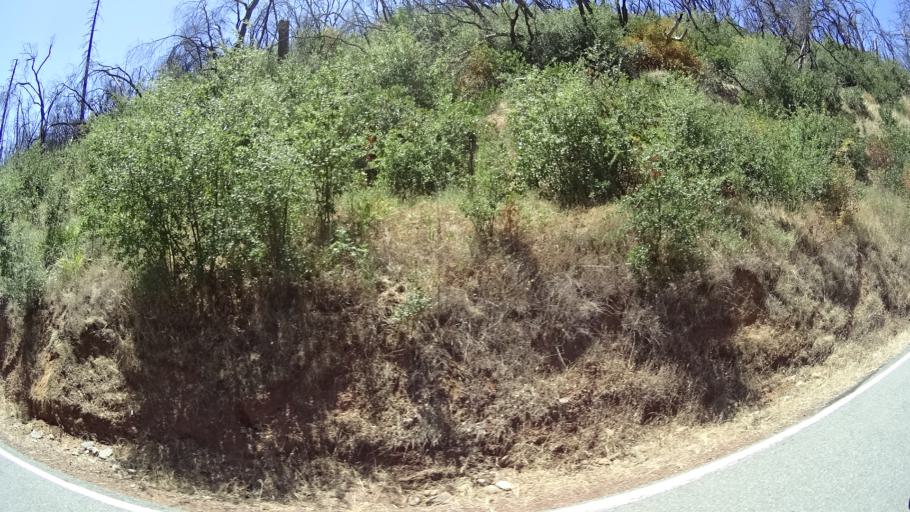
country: US
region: California
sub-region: Calaveras County
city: San Andreas
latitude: 38.2895
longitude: -120.6711
